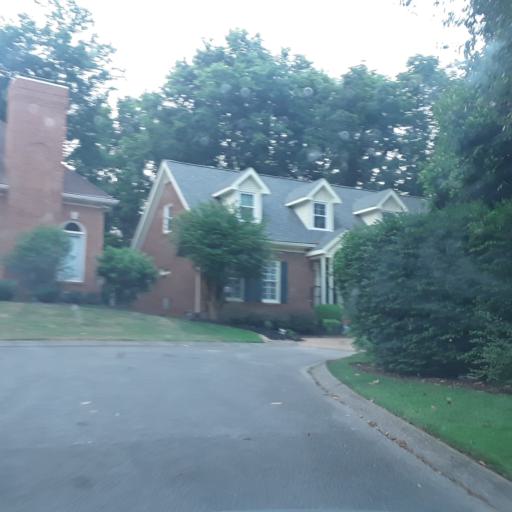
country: US
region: Tennessee
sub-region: Williamson County
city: Brentwood
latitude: 36.0471
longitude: -86.7657
